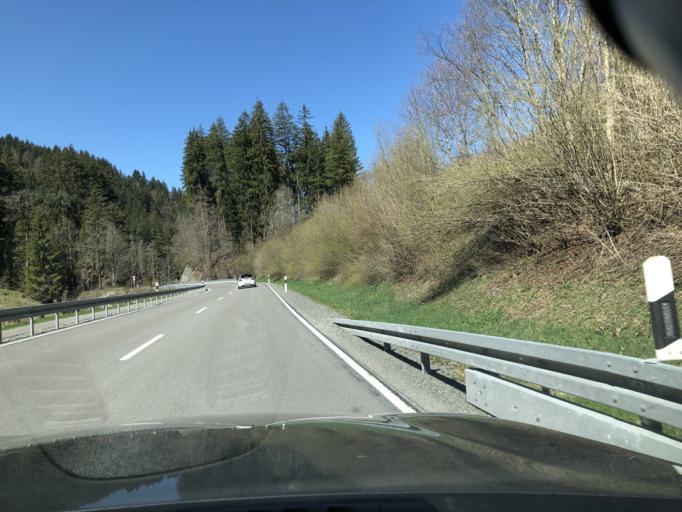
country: DE
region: Bavaria
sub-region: Swabia
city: Wertach
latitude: 47.5828
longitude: 10.4130
